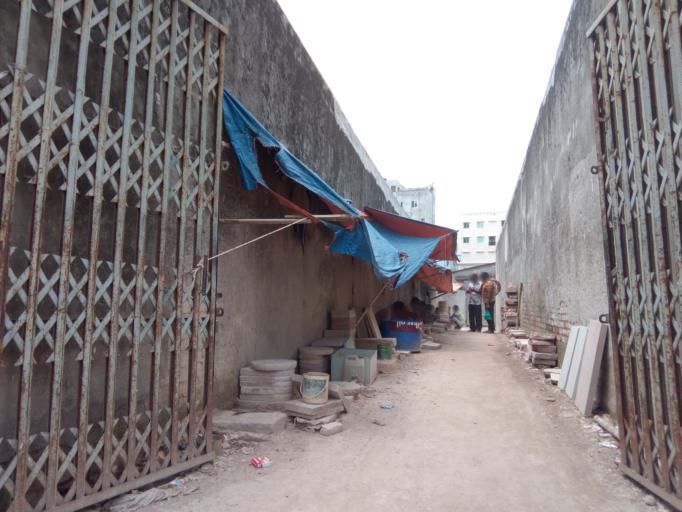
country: BD
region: Dhaka
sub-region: Dhaka
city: Dhaka
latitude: 23.7115
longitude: 90.3963
